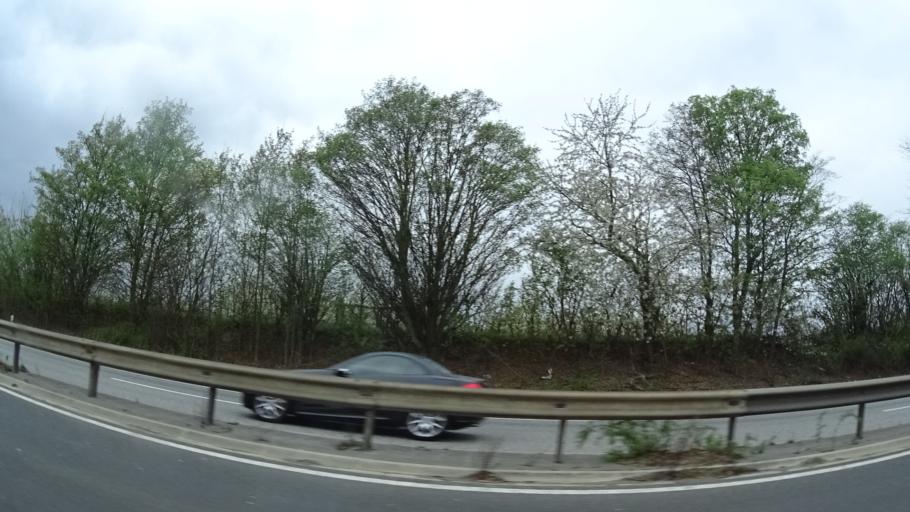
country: DE
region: Rheinland-Pfalz
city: Klein-Winternheim
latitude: 49.9779
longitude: 8.2117
